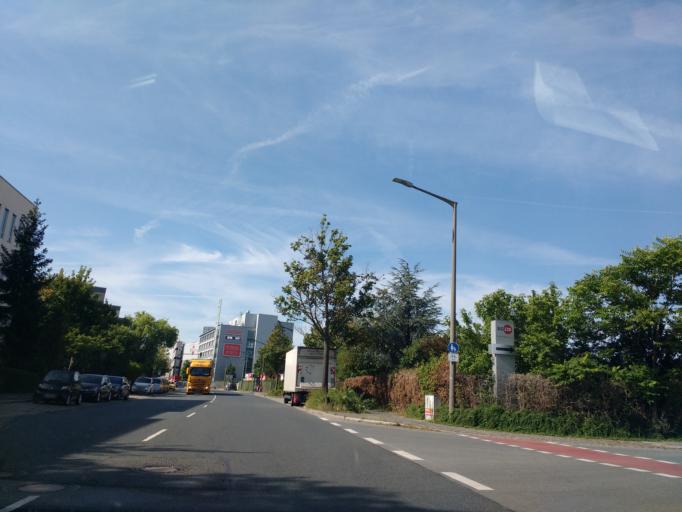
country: DE
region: Bavaria
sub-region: Regierungsbezirk Mittelfranken
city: Grossreuth bei Schweinau
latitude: 49.4435
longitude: 11.0058
